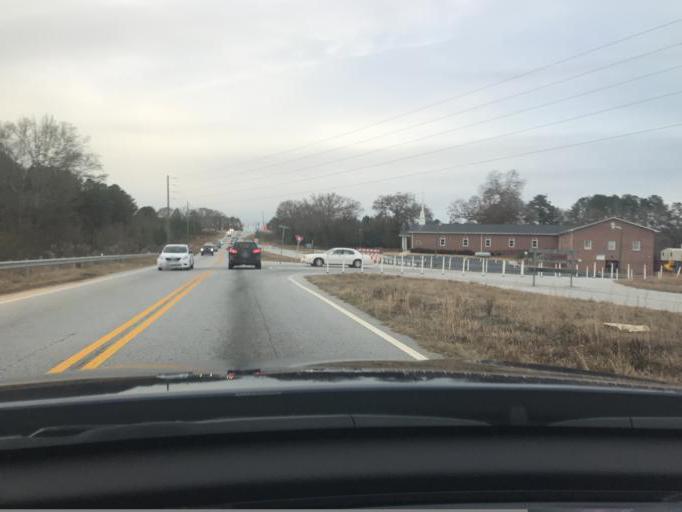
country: US
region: Georgia
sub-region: Newton County
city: Porterdale
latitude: 33.6108
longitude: -83.9195
